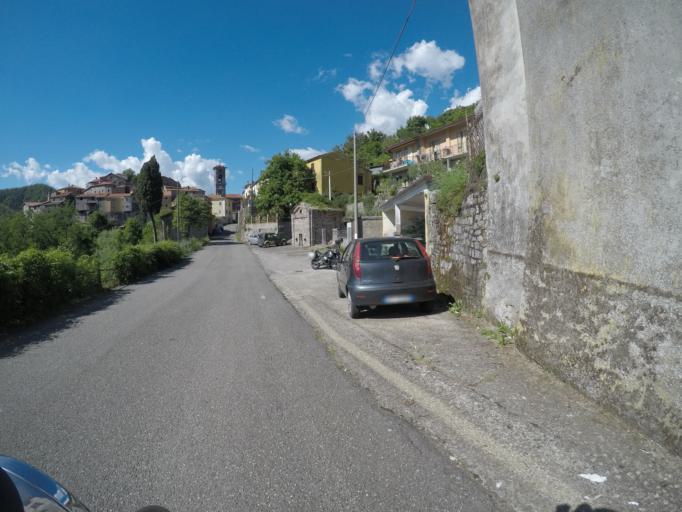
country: IT
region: Tuscany
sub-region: Provincia di Massa-Carrara
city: Fosdinovo
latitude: 44.1518
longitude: 10.1027
